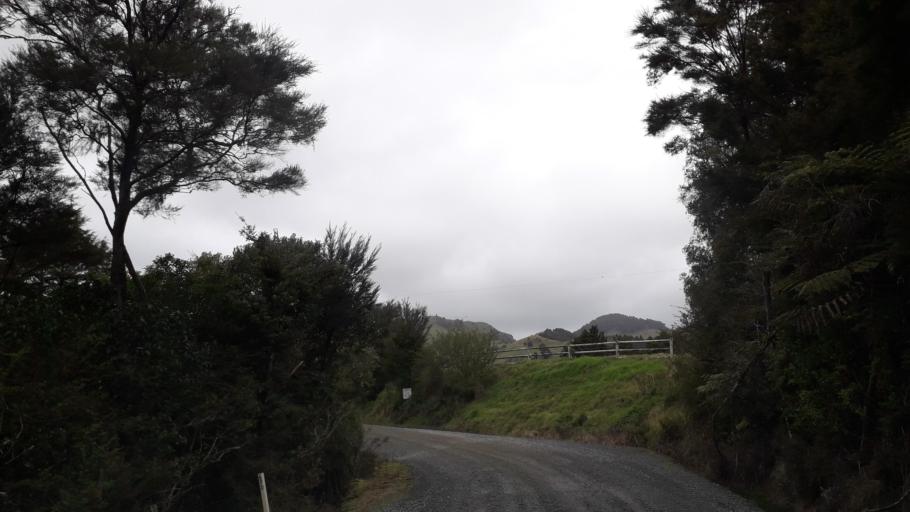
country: NZ
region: Northland
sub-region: Far North District
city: Kerikeri
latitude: -35.1312
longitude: 173.7292
